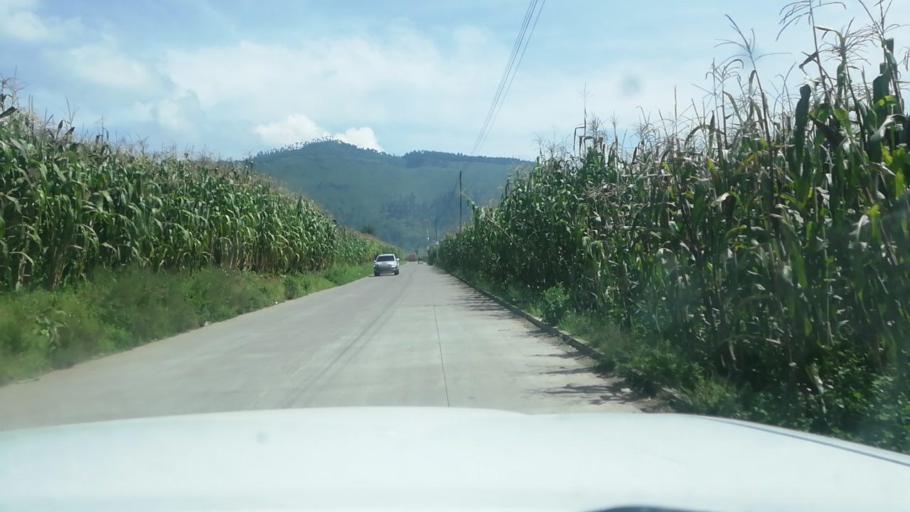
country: GT
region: Totonicapan
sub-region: Municipio de San Andres Xecul
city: San Andres Xecul
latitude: 14.8943
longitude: -91.4776
